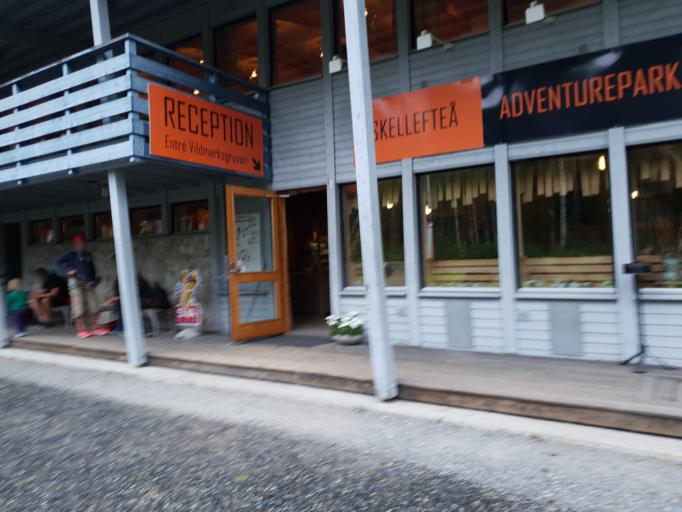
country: SE
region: Vaesterbotten
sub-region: Skelleftea Kommun
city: Viken
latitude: 64.8012
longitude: 20.7426
